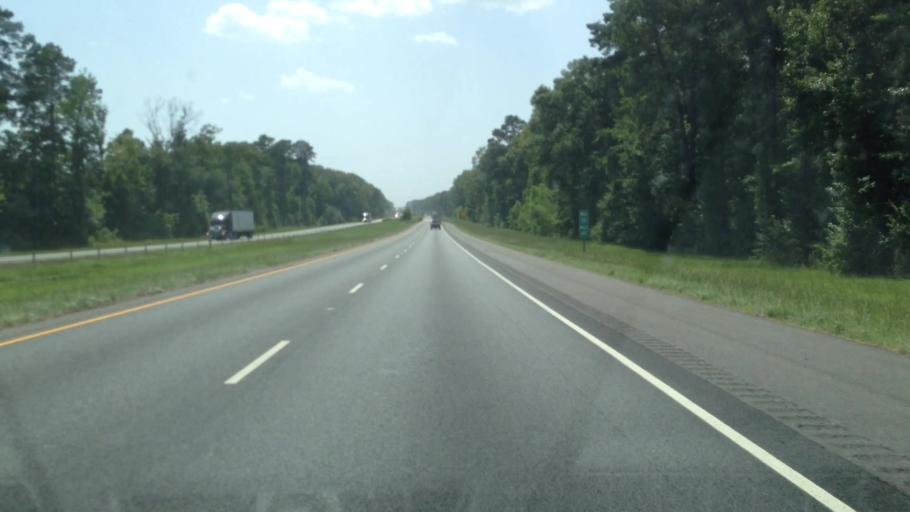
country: US
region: Louisiana
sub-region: Bienville Parish
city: Arcadia
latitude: 32.5636
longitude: -93.0796
